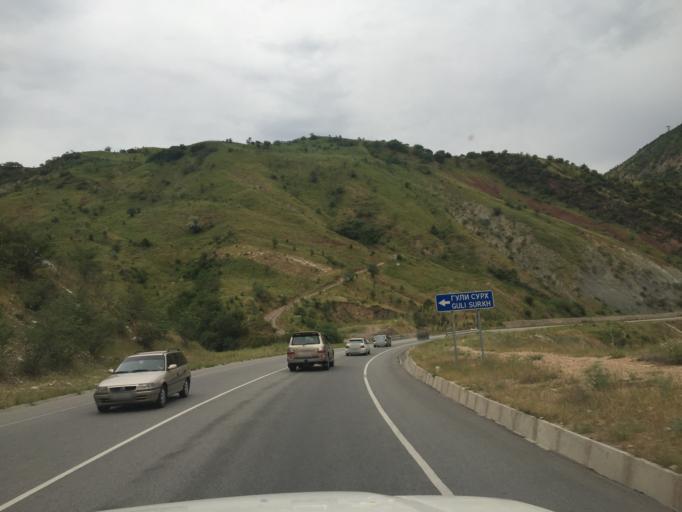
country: TJ
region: Khatlon
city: Norak
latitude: 38.4358
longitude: 69.2070
